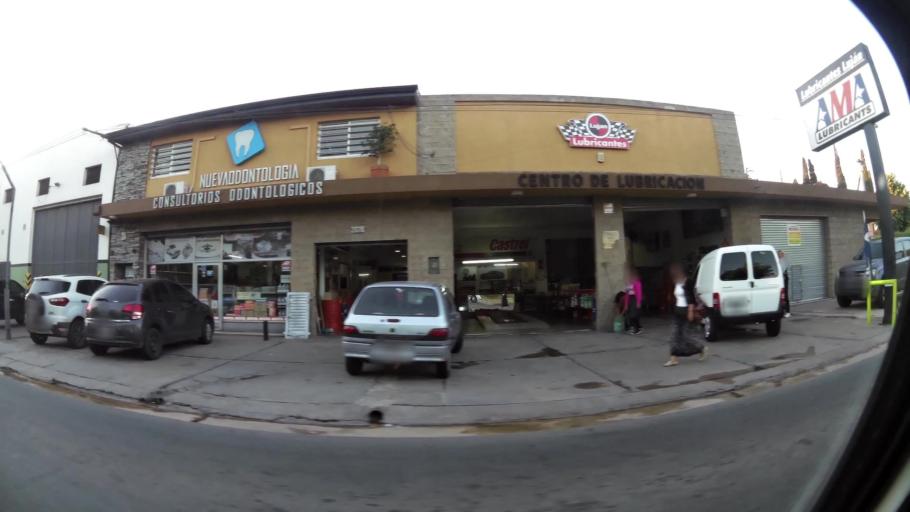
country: AR
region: Buenos Aires
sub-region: Partido de Quilmes
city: Quilmes
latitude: -34.8150
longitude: -58.1917
